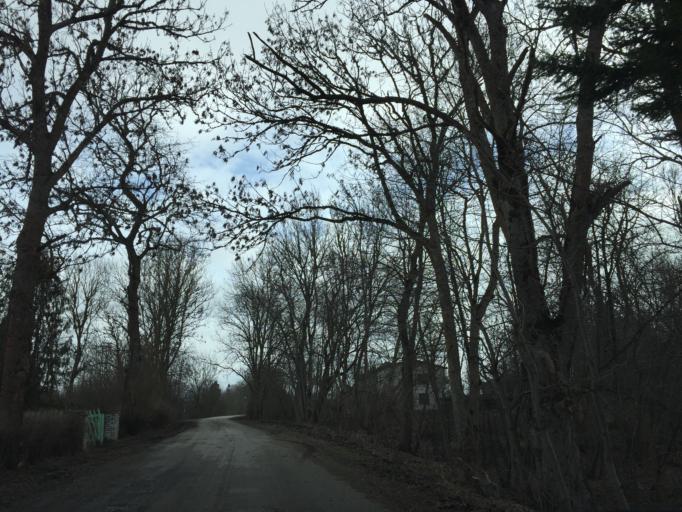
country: EE
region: Laeaene
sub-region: Lihula vald
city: Lihula
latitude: 58.7349
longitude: 23.8586
